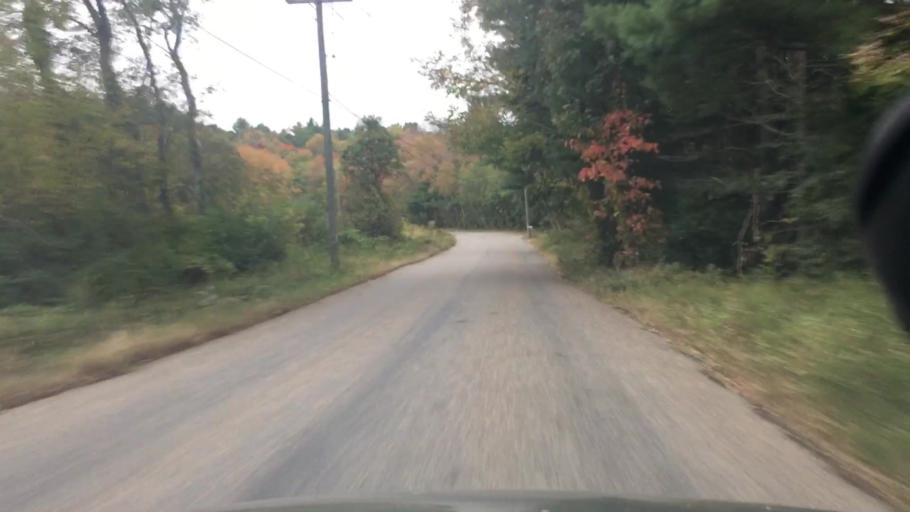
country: US
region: Connecticut
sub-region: Tolland County
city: Stafford
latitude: 41.9691
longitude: -72.2876
